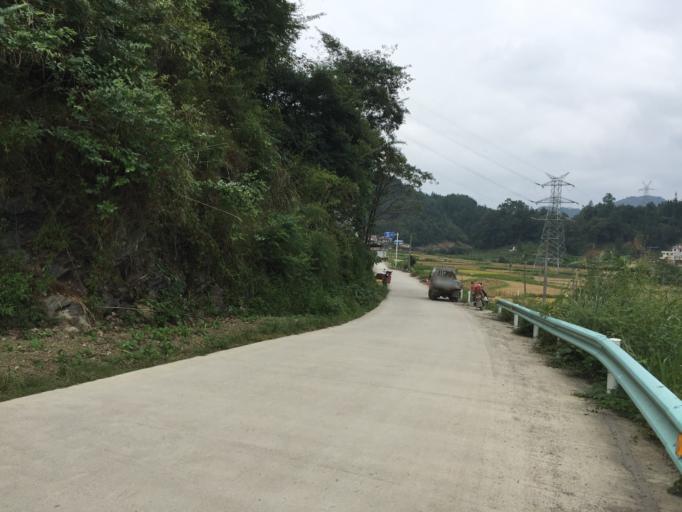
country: CN
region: Guizhou Sheng
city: Duyun
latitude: 26.3420
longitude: 107.5371
